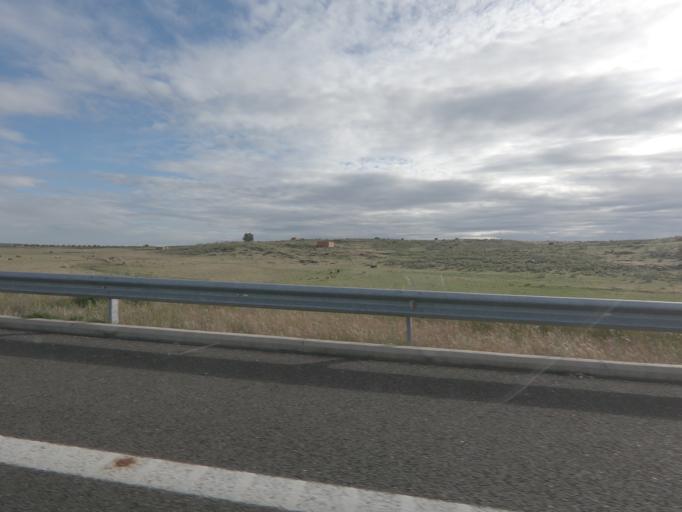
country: ES
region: Extremadura
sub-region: Provincia de Caceres
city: Casas de Don Gomez
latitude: 40.0185
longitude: -6.5903
